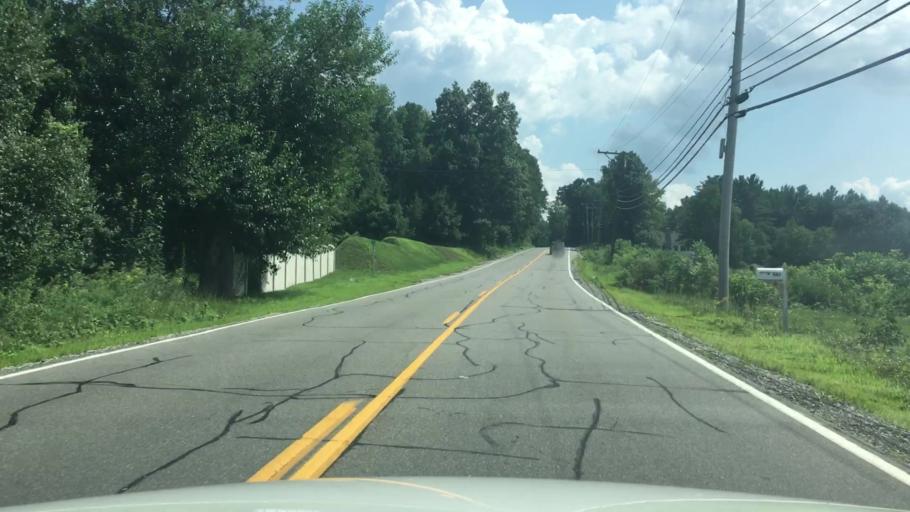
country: US
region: New Hampshire
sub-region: Rockingham County
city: Auburn
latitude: 42.9771
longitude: -71.3685
